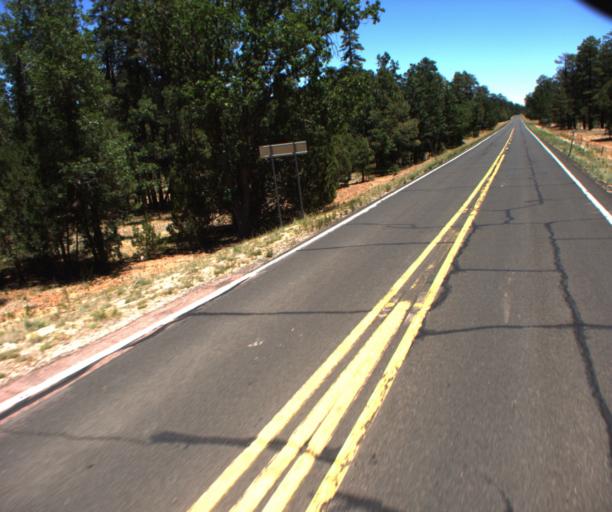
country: US
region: Arizona
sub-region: Gila County
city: Star Valley
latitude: 34.6241
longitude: -111.1540
